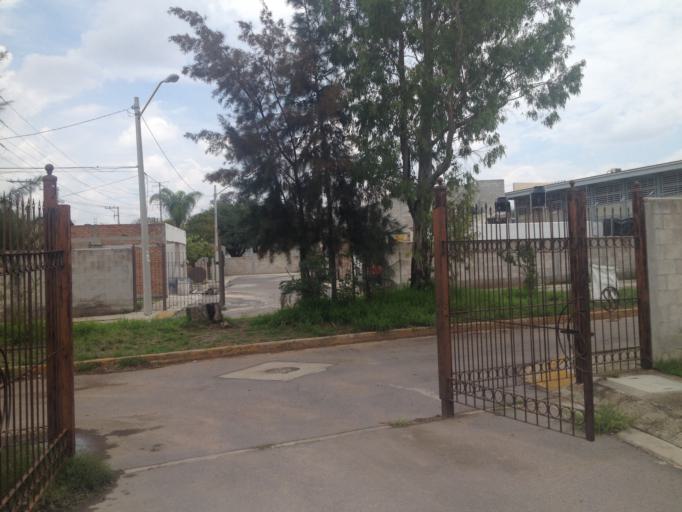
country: MX
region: Aguascalientes
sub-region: Aguascalientes
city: San Sebastian [Fraccionamiento]
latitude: 21.8190
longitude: -102.2707
